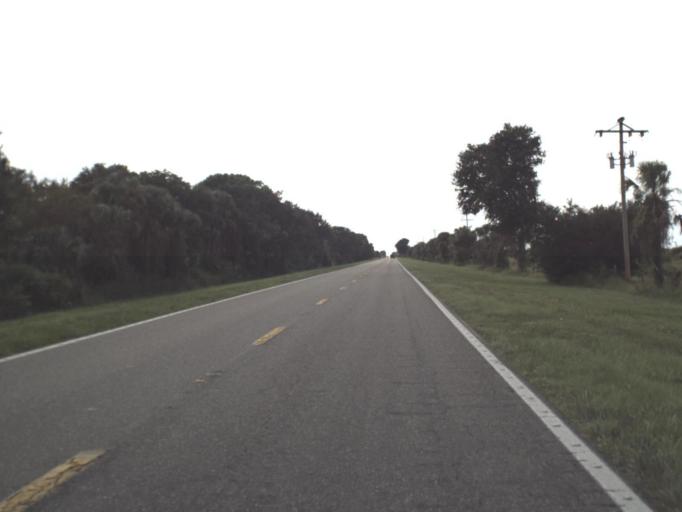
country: US
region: Florida
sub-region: Hendry County
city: Port LaBelle
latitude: 26.7685
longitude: -81.2806
